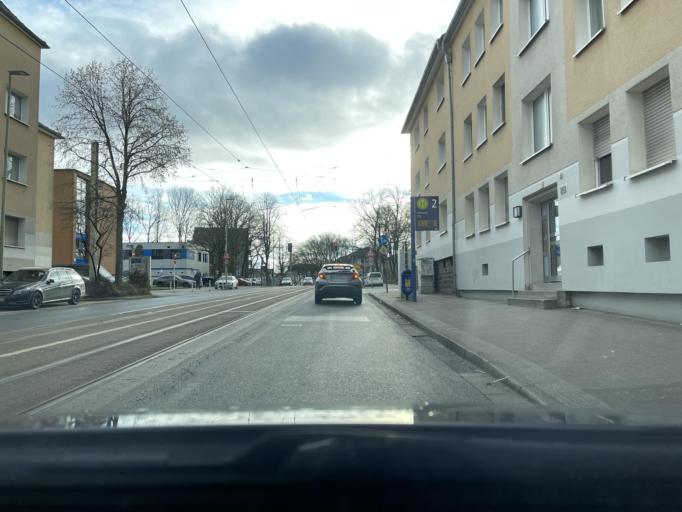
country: DE
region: North Rhine-Westphalia
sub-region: Regierungsbezirk Dusseldorf
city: Essen
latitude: 51.4402
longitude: 6.9883
